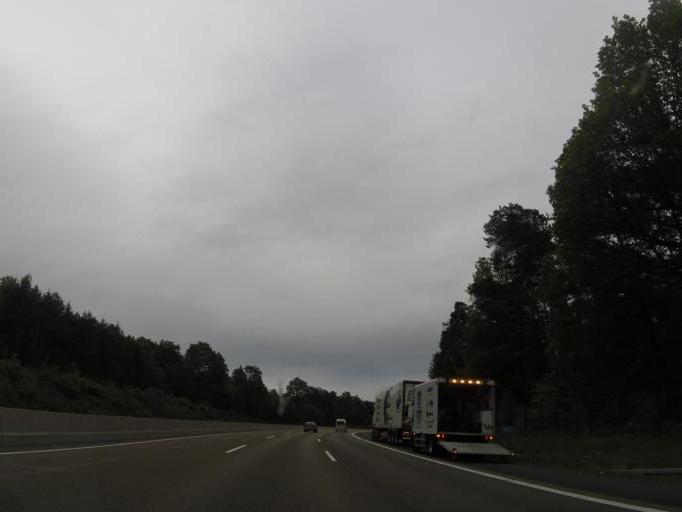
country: DE
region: Hesse
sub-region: Regierungsbezirk Kassel
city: Kirchheim
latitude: 50.8861
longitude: 9.5941
